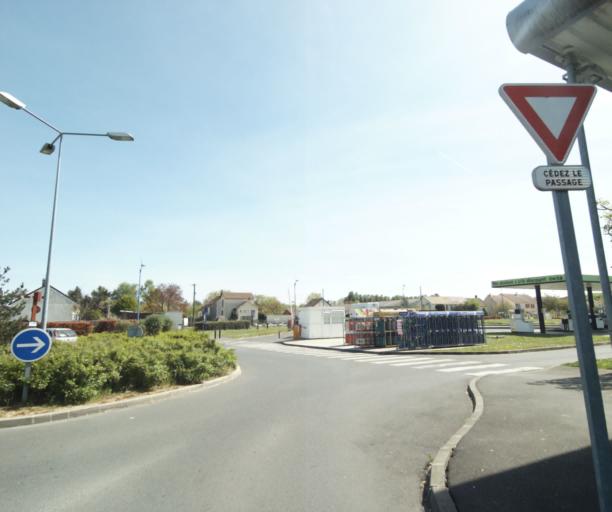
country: FR
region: Ile-de-France
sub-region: Departement de Seine-et-Marne
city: Nangis
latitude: 48.5558
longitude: 3.0046
